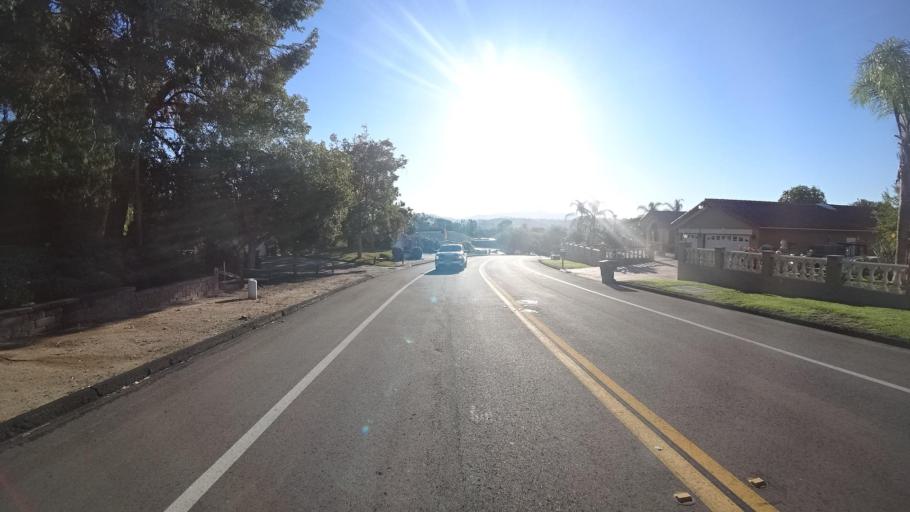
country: US
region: California
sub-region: San Diego County
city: Bonita
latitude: 32.6719
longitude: -117.0322
